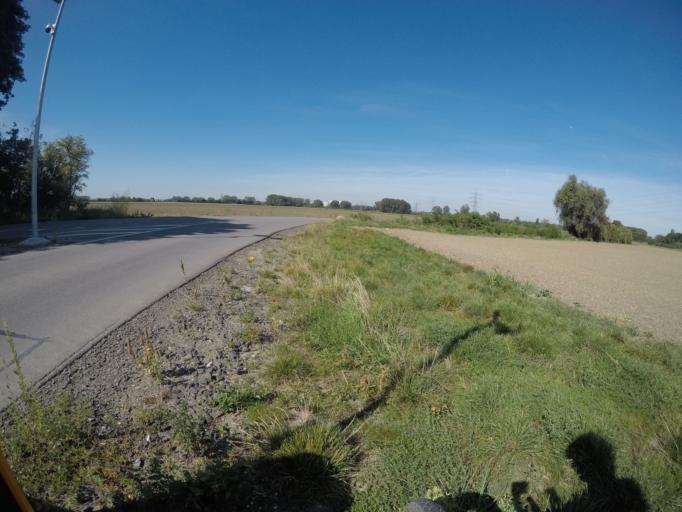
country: DE
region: Hesse
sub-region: Regierungsbezirk Darmstadt
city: Biblis
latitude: 49.6962
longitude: 8.4437
